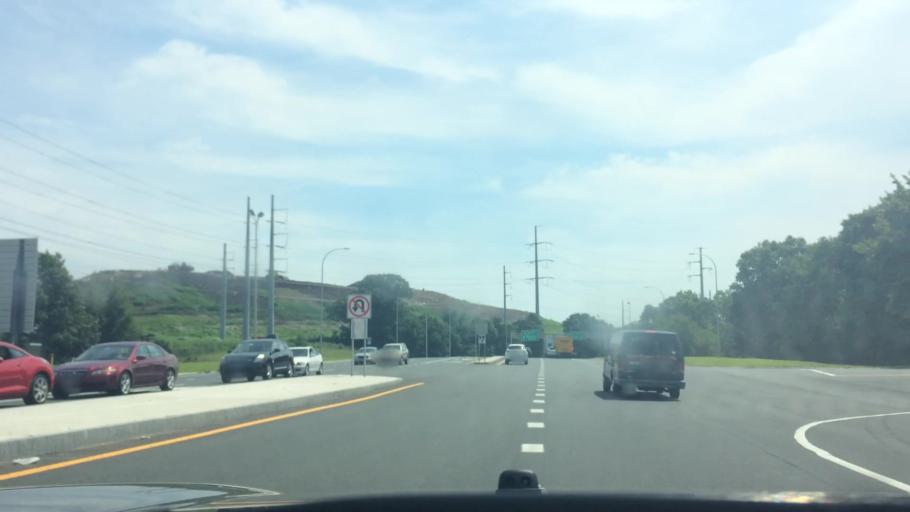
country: US
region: Massachusetts
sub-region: Hampden County
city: North Chicopee
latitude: 42.1638
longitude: -72.5455
